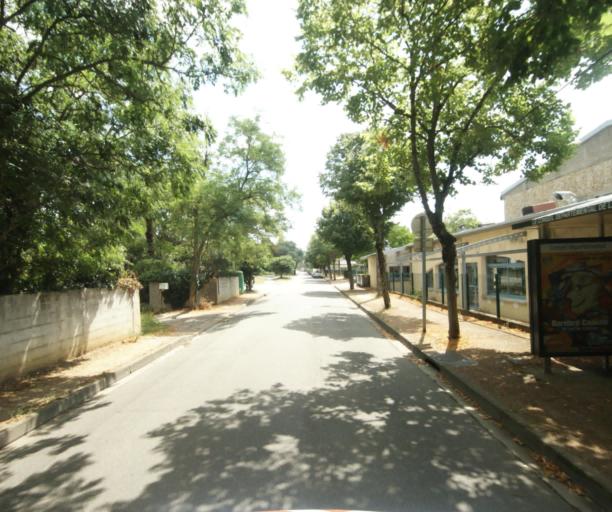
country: FR
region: Midi-Pyrenees
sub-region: Departement de la Haute-Garonne
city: Revel
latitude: 43.4613
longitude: 2.0079
